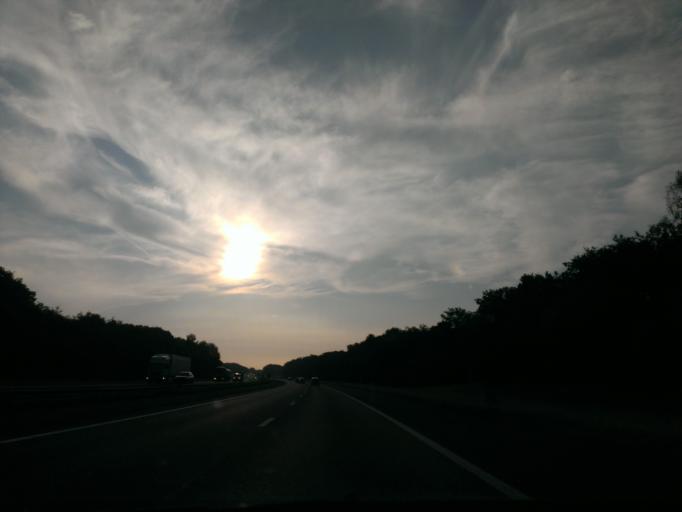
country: NL
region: Overijssel
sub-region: Gemeente Hof van Twente
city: Markelo
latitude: 52.2830
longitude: 6.5401
